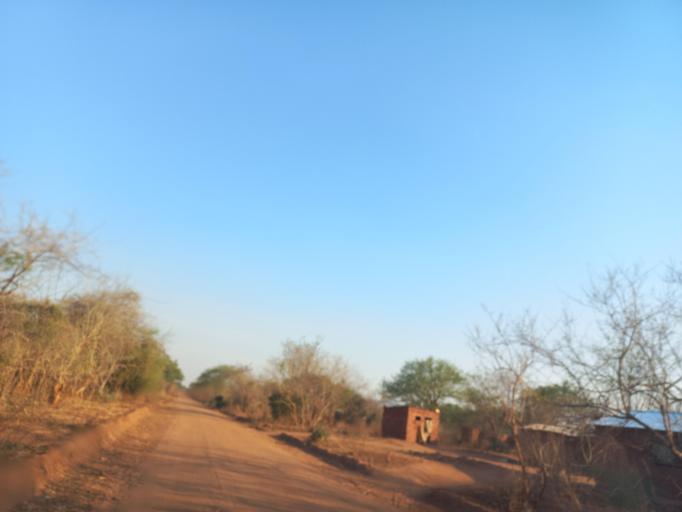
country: ZM
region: Lusaka
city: Luangwa
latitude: -15.4384
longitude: 30.3578
